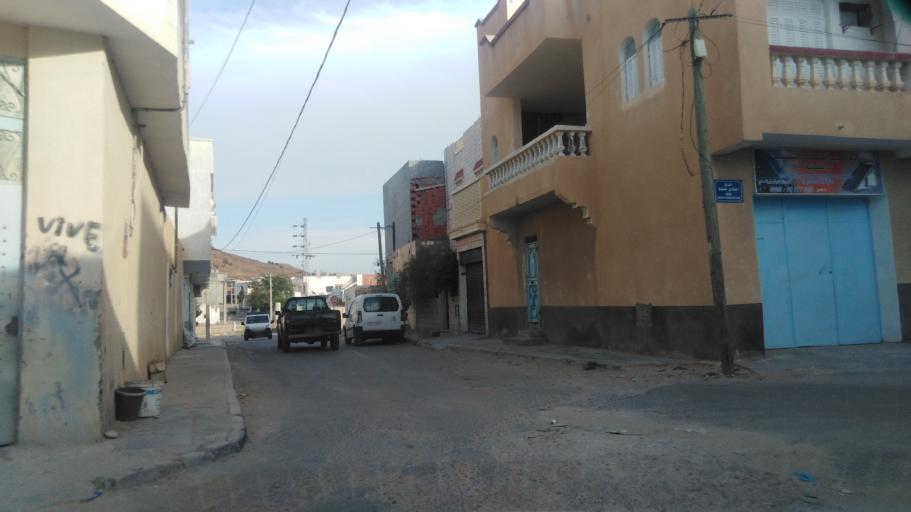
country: TN
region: Tataouine
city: Tataouine
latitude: 32.9374
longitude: 10.4561
